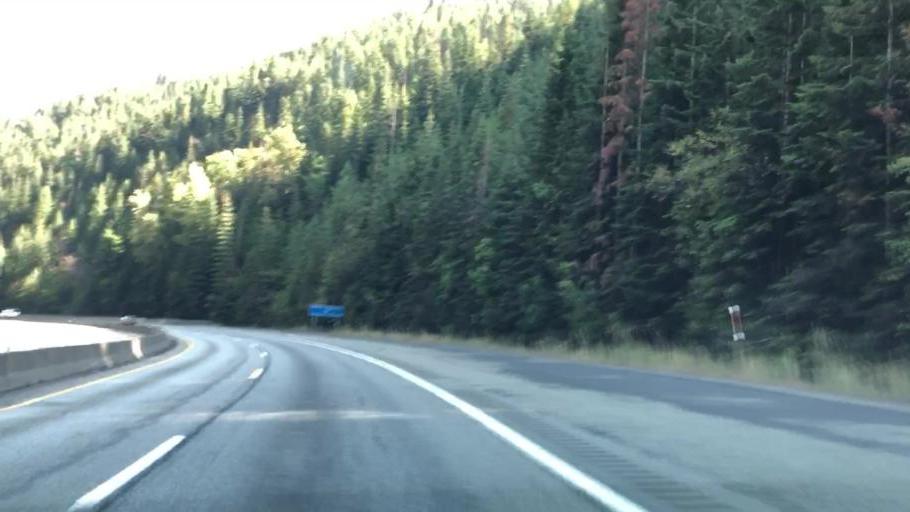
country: US
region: Idaho
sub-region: Shoshone County
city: Pinehurst
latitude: 47.5916
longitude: -116.4920
